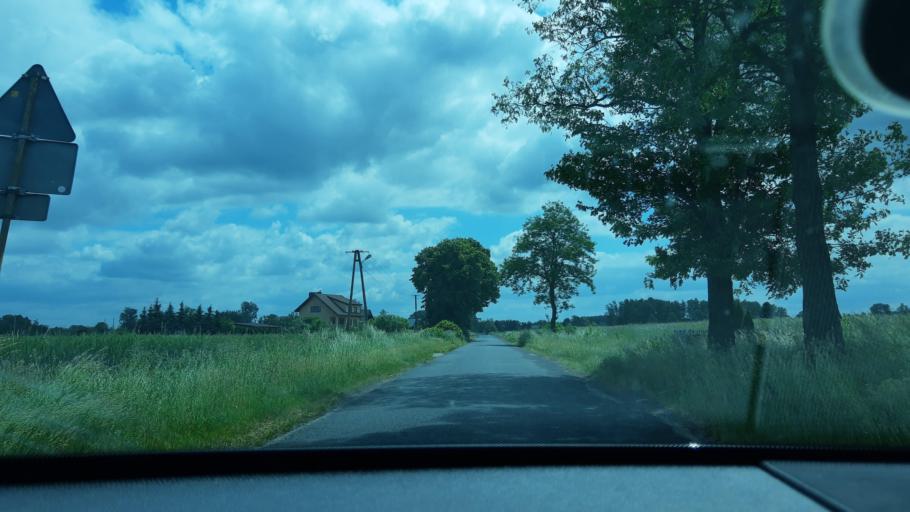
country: PL
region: Lodz Voivodeship
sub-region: Powiat zdunskowolski
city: Zapolice
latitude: 51.5381
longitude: 18.8264
